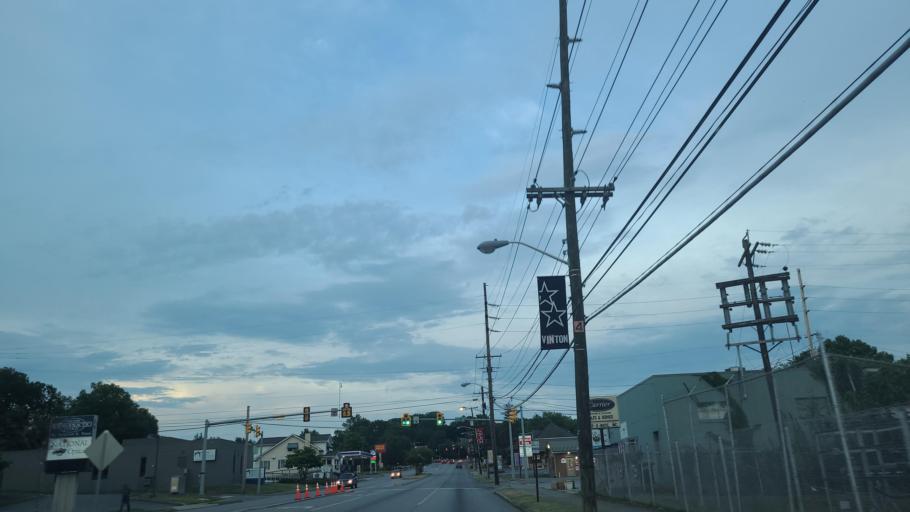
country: US
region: Virginia
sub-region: Roanoke County
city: Vinton
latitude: 37.2762
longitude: -79.9040
